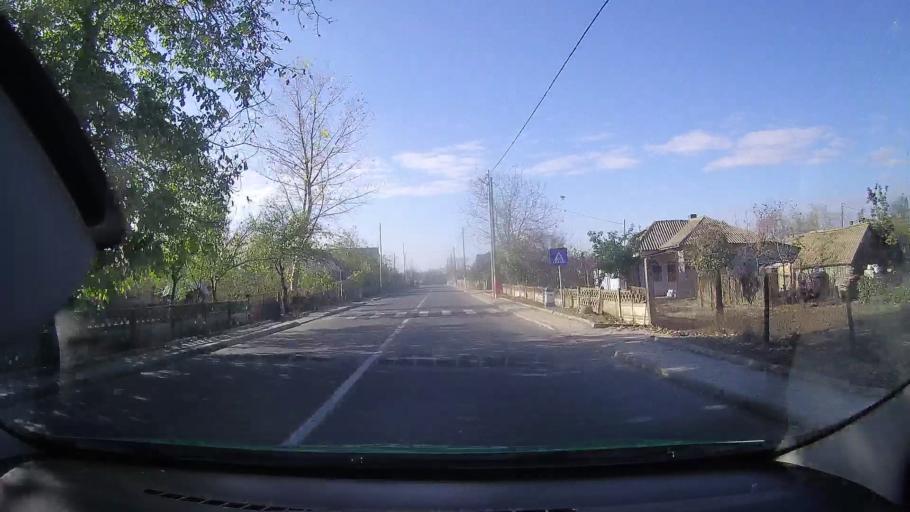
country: RO
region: Tulcea
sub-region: Comuna Murighiol
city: Murighiol
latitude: 45.0222
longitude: 29.1283
